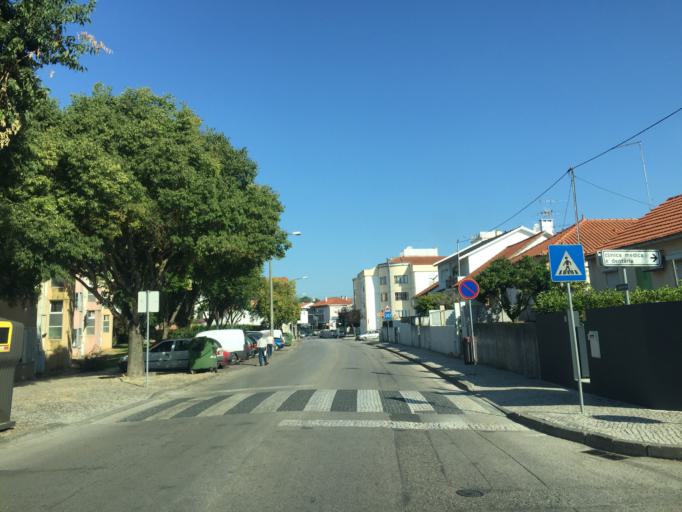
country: PT
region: Santarem
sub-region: Tomar
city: Tomar
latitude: 39.6033
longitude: -8.4007
